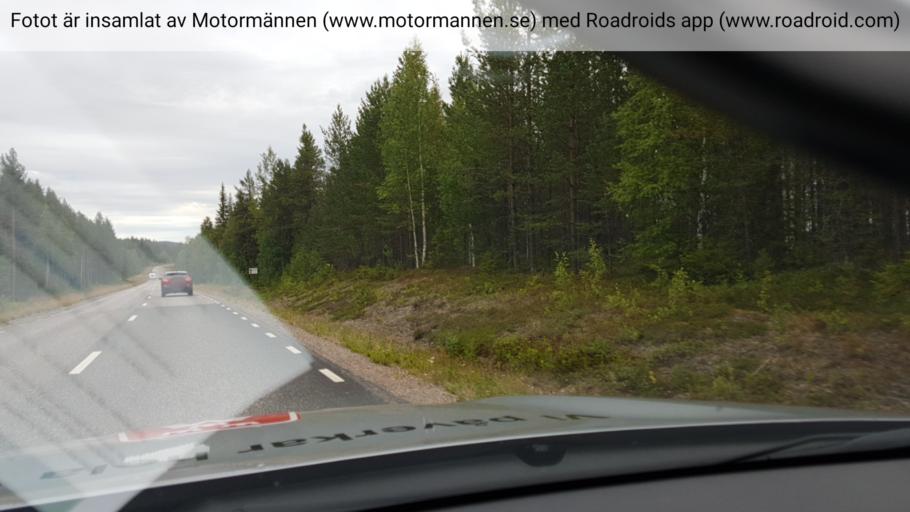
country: SE
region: Norrbotten
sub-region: Overkalix Kommun
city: OEverkalix
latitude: 66.5261
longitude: 22.7594
